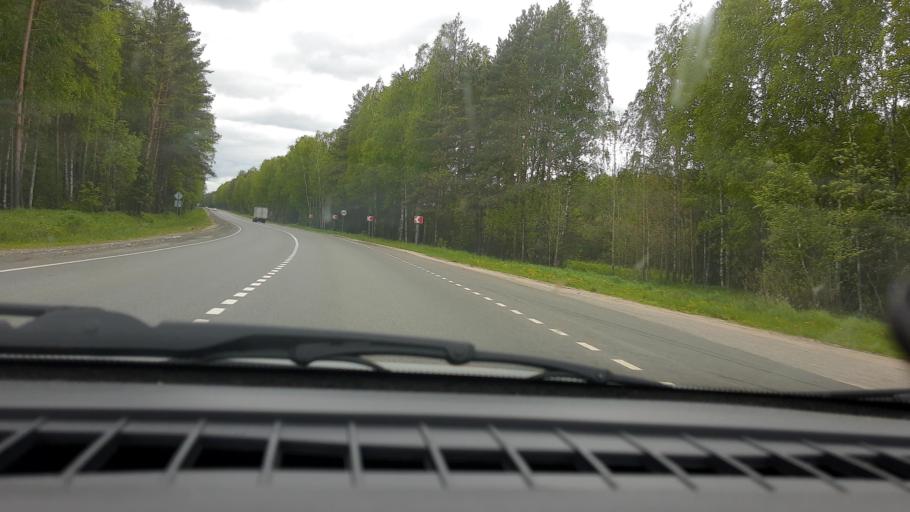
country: RU
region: Nizjnij Novgorod
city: Semenov
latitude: 56.7269
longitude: 44.2900
